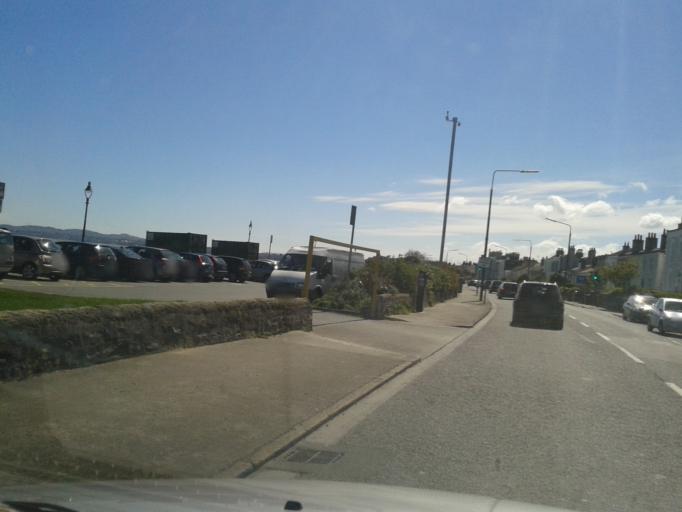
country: IE
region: Leinster
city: Sandymount
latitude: 53.3286
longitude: -6.2088
